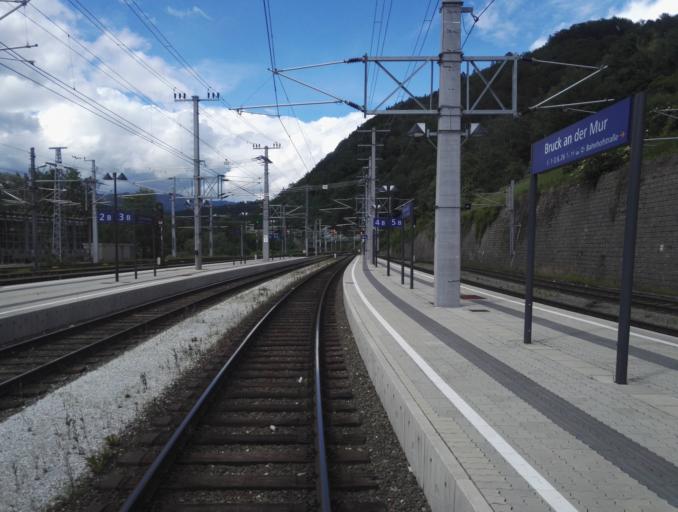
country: AT
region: Styria
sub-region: Politischer Bezirk Bruck-Muerzzuschlag
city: Bruck an der Mur
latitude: 47.4155
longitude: 15.2794
